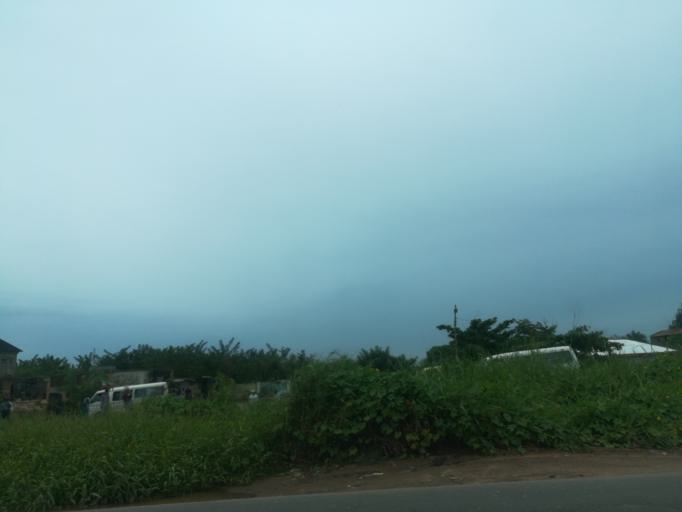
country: NG
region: Oyo
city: Ibadan
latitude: 7.3565
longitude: 3.9227
